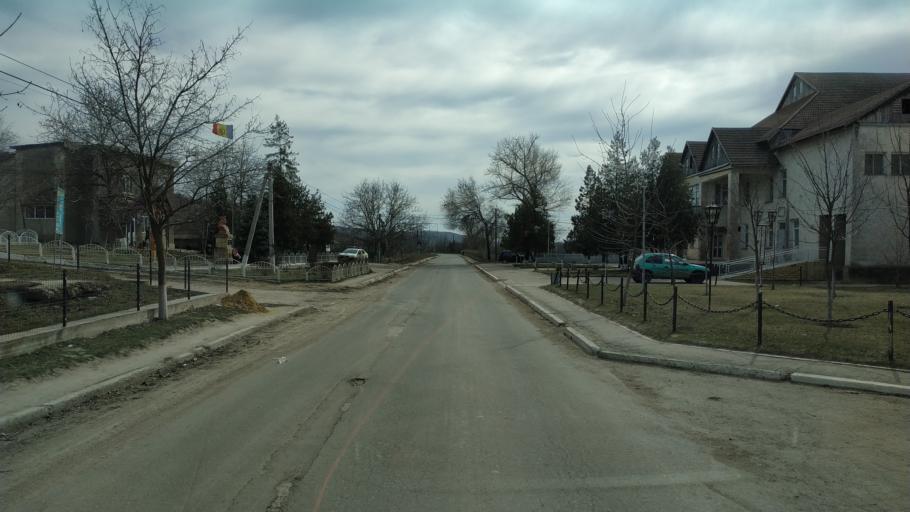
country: MD
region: Nisporeni
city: Nisporeni
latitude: 46.9673
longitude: 28.2135
